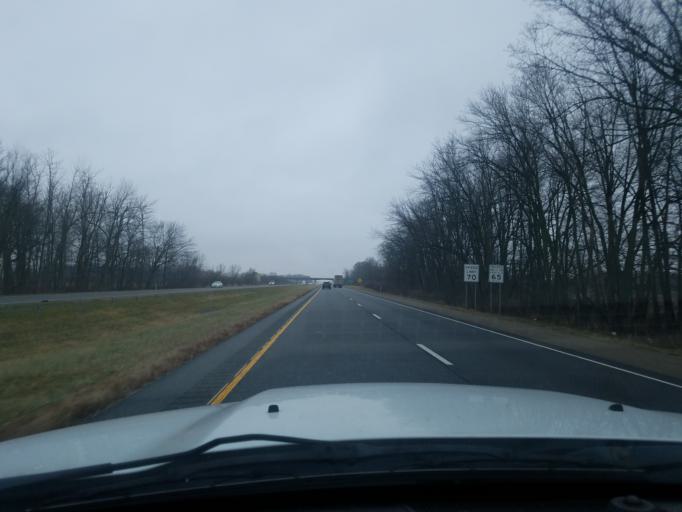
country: US
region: Indiana
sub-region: Madison County
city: Alexandria
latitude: 40.2866
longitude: -85.5580
